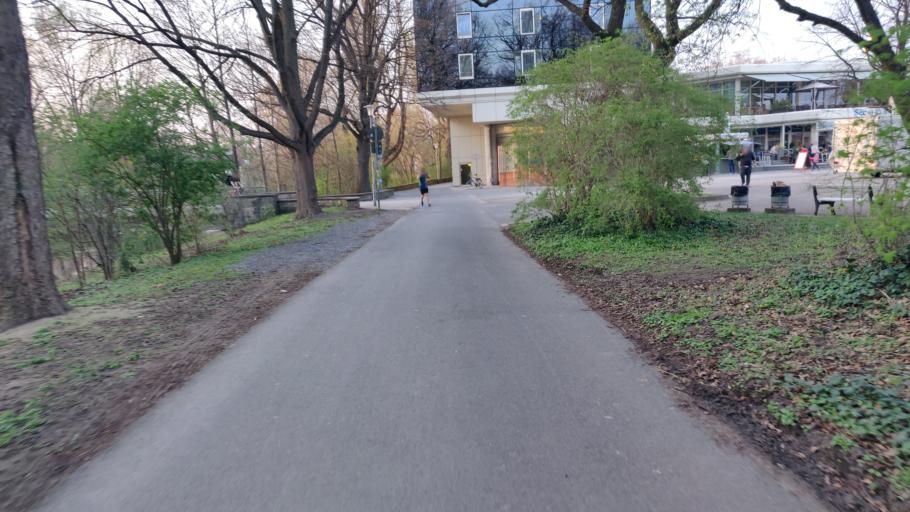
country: DE
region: Lower Saxony
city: Hannover
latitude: 52.3611
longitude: 9.7346
